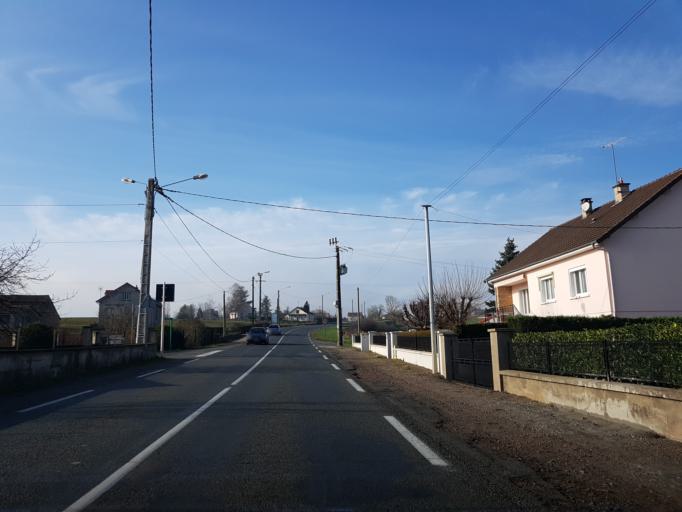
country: FR
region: Bourgogne
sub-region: Departement de Saone-et-Loire
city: Gueugnon
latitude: 46.5955
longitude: 4.0409
